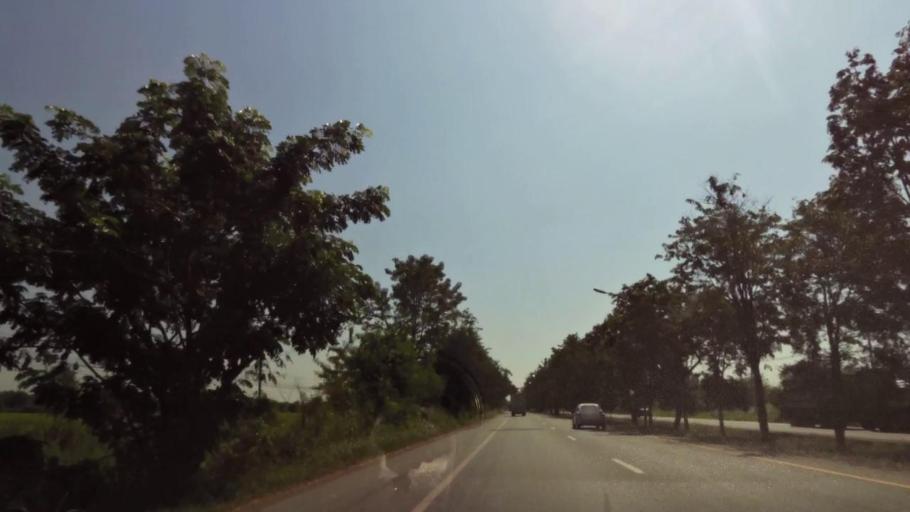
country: TH
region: Nakhon Sawan
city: Kao Liao
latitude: 15.9091
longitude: 100.1124
